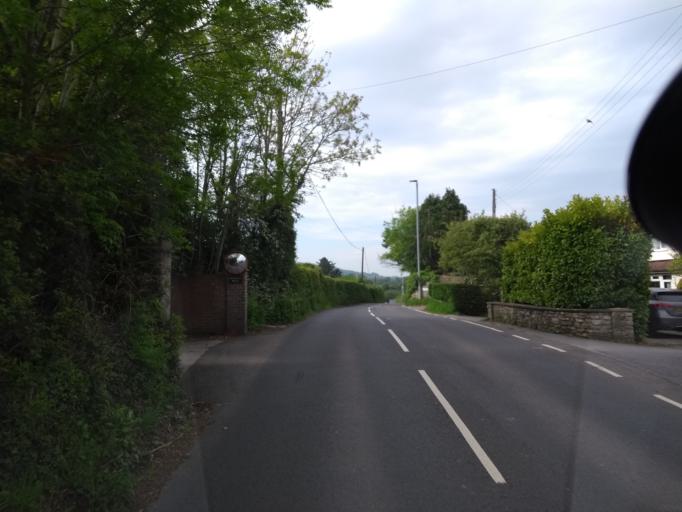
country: GB
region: England
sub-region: Devon
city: Axminster
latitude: 50.7741
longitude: -3.0039
